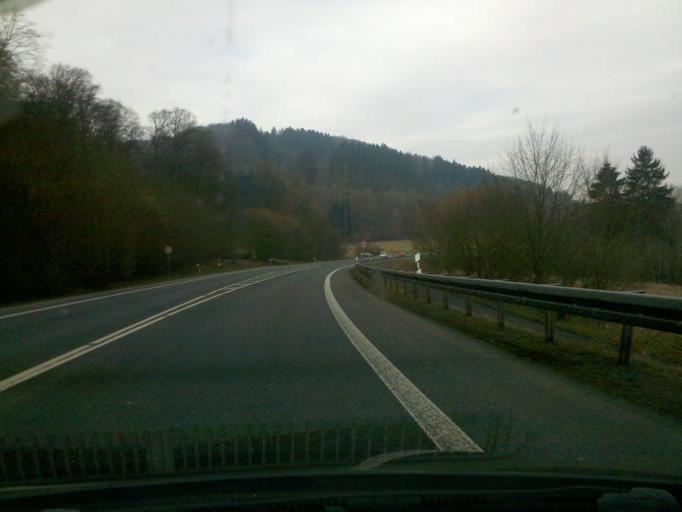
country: DE
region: Hesse
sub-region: Regierungsbezirk Giessen
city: Haiger
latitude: 50.7385
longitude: 8.2354
